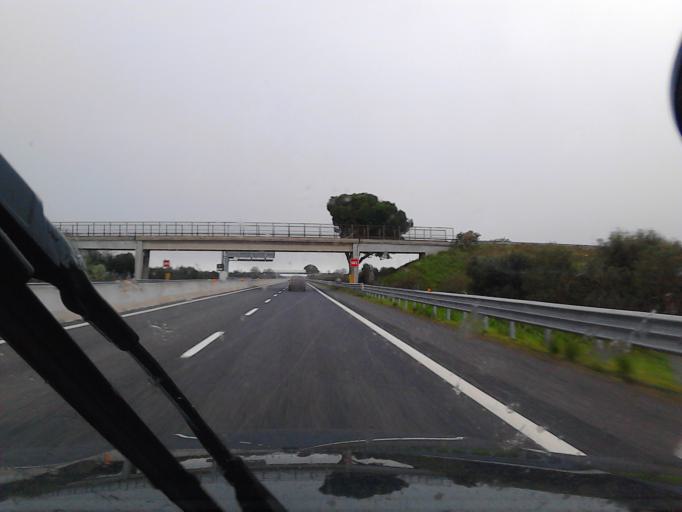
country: IT
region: Apulia
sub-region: Provincia di Bari
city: Giovinazzo
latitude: 41.1503
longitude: 16.6624
